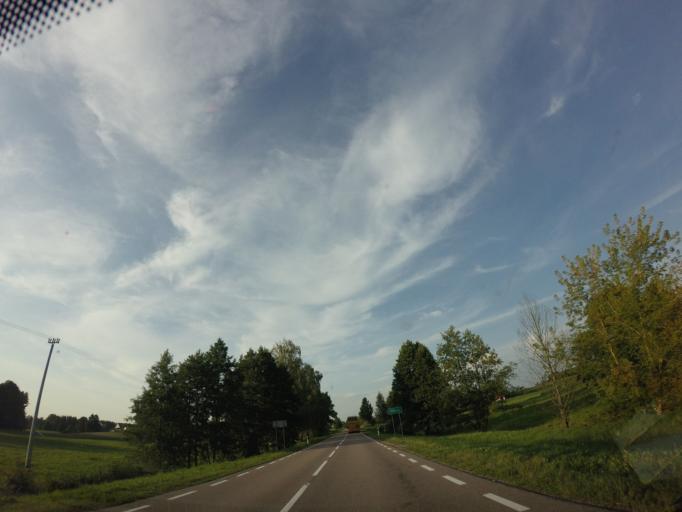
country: PL
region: Podlasie
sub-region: Powiat sejnenski
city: Sejny
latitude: 54.0683
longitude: 23.3629
